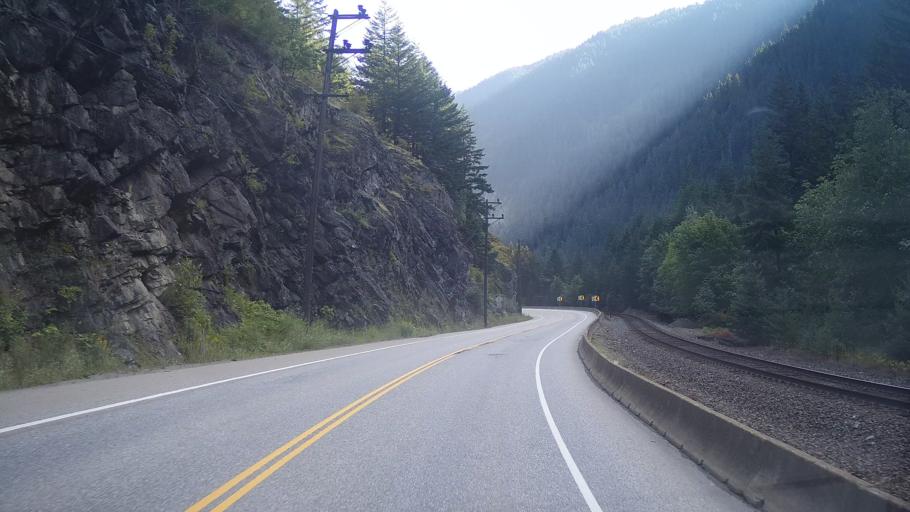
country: CA
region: British Columbia
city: Hope
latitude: 49.6223
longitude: -121.3982
